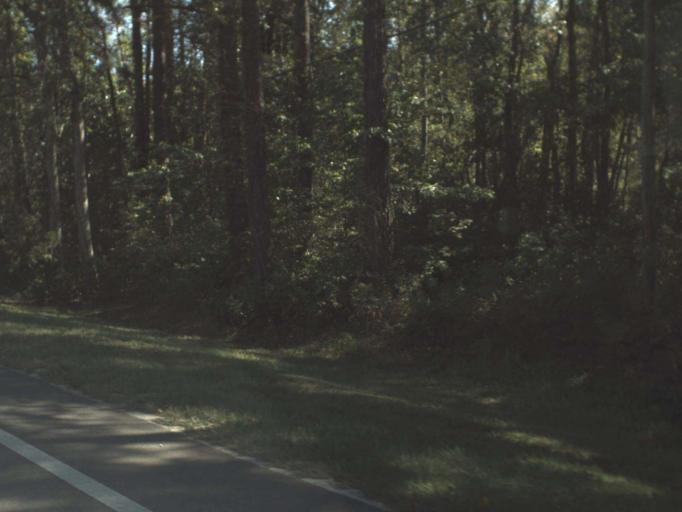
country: US
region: Florida
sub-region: Walton County
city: Freeport
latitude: 30.4953
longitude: -86.1303
